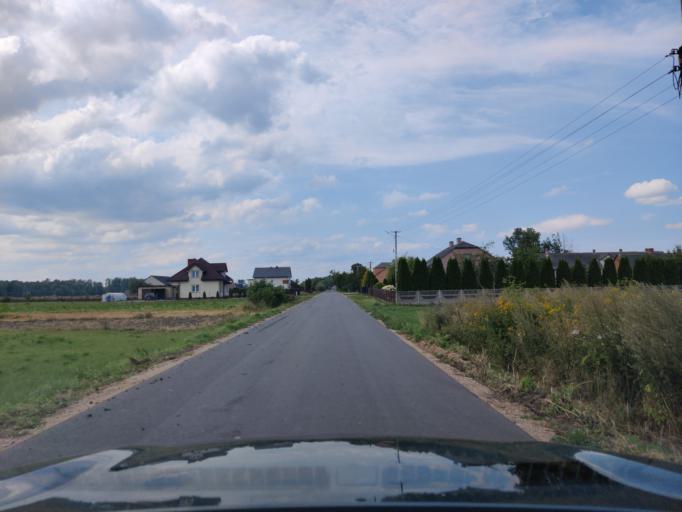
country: PL
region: Masovian Voivodeship
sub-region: Powiat pultuski
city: Obryte
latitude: 52.6894
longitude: 21.2271
